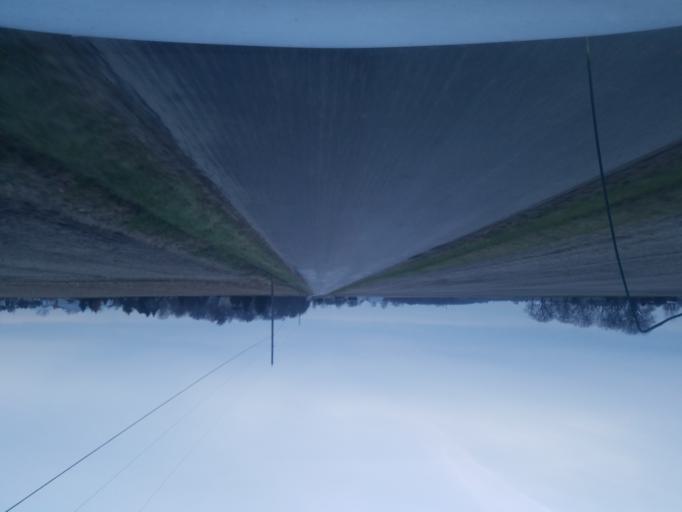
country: US
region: Indiana
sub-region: Adams County
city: Decatur
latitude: 40.7884
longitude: -84.9525
